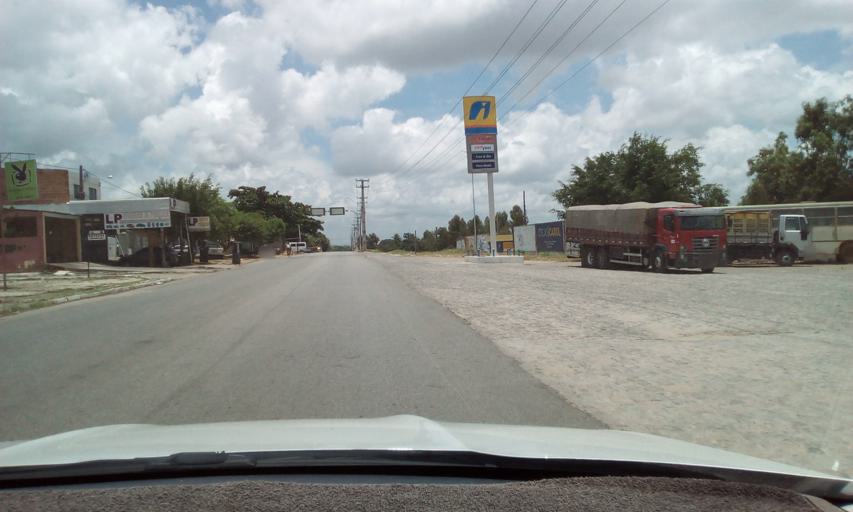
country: BR
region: Pernambuco
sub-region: Bonito
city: Bonito
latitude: -8.4641
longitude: -35.7301
